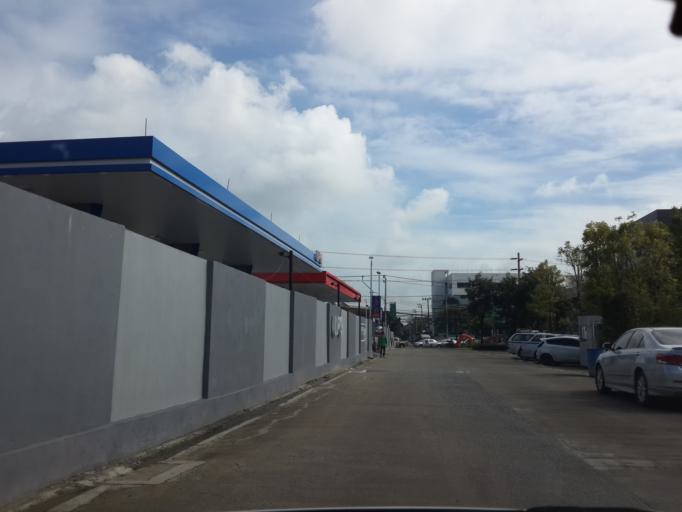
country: TH
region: Bangkok
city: Wang Thonglang
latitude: 13.7666
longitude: 100.6004
